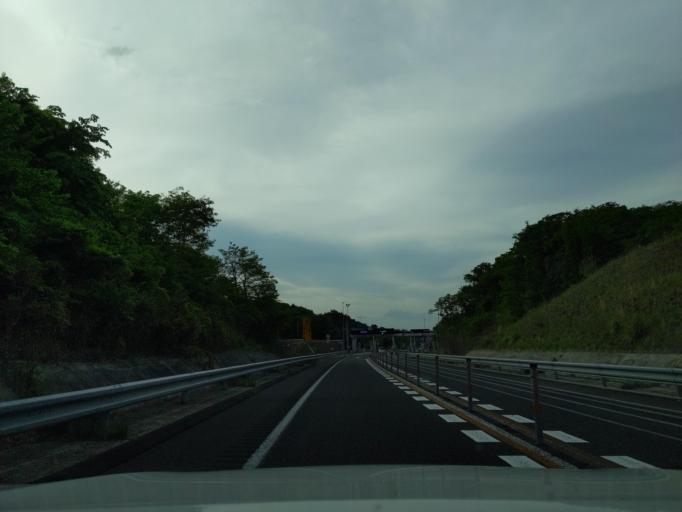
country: JP
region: Miyagi
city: Tomiya
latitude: 38.3794
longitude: 140.8823
